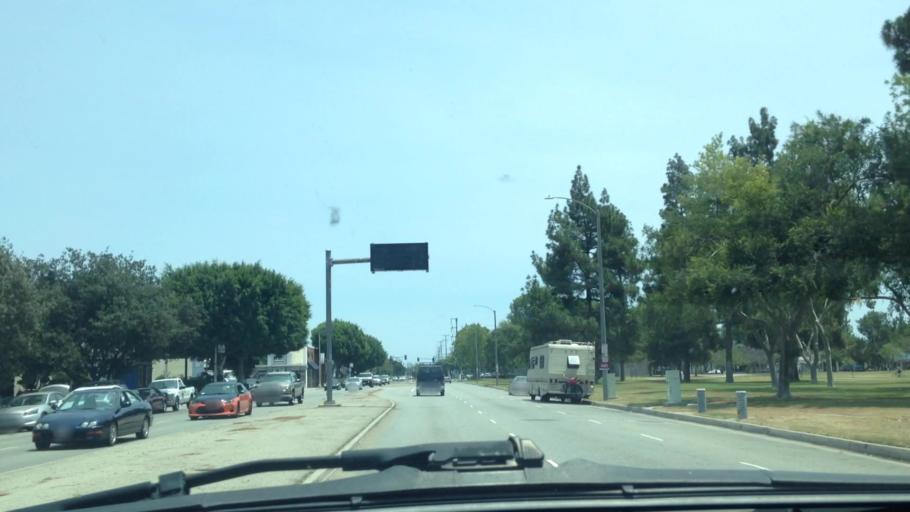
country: US
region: California
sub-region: Los Angeles County
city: Lakewood
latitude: 33.8323
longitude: -118.1284
